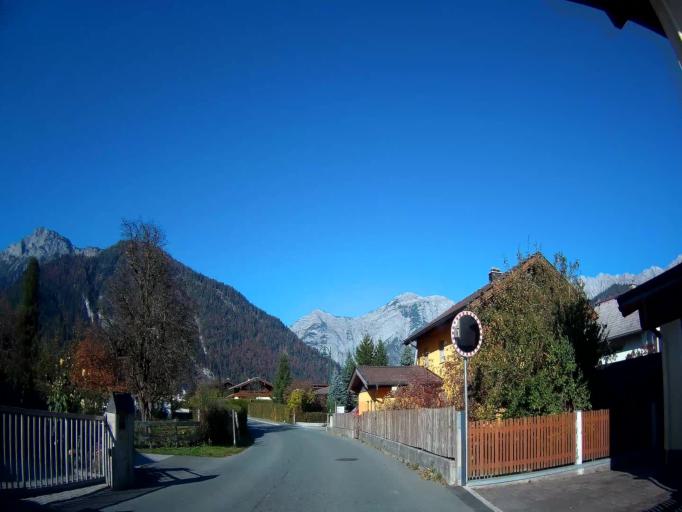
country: AT
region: Salzburg
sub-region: Politischer Bezirk Zell am See
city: Saalfelden am Steinernen Meer
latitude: 47.4446
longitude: 12.8184
